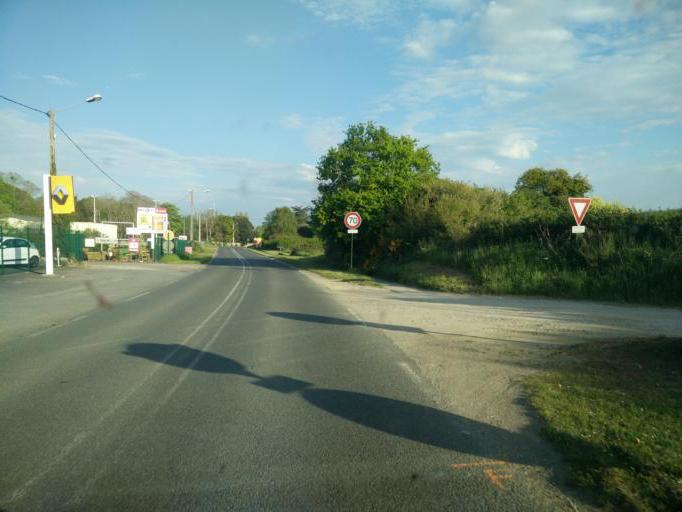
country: FR
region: Brittany
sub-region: Departement des Cotes-d'Armor
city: Erquy
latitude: 48.6236
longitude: -2.4415
